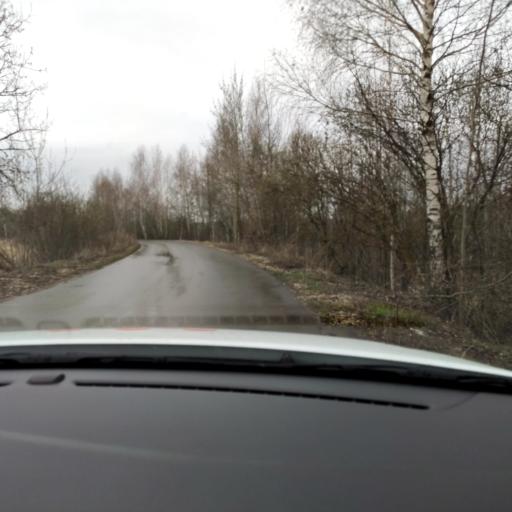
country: RU
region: Tatarstan
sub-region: Gorod Kazan'
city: Kazan
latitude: 55.6952
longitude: 49.0741
